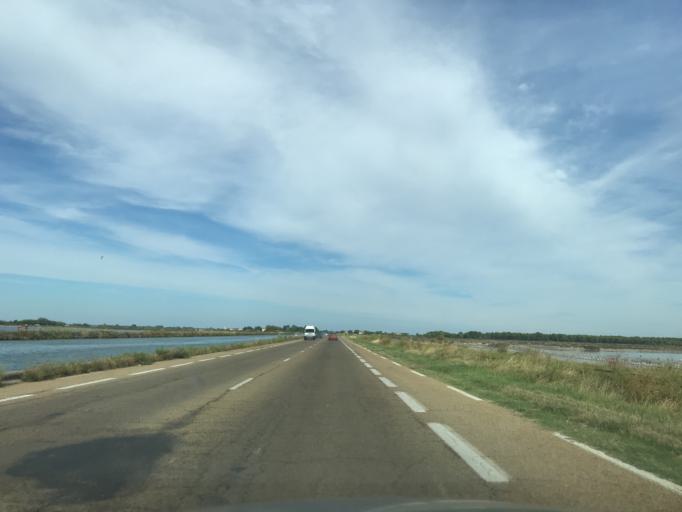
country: FR
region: Languedoc-Roussillon
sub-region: Departement du Gard
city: Le Grau-du-Roi
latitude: 43.5436
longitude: 4.1515
